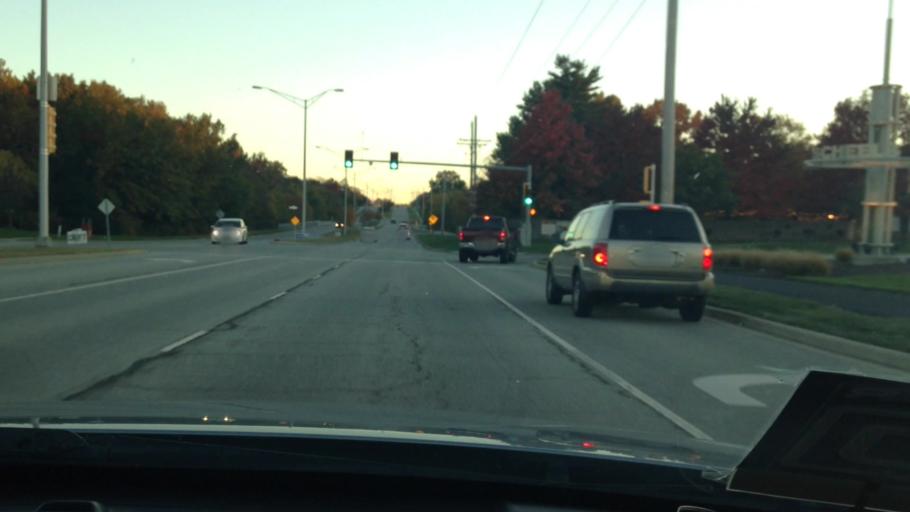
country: US
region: Kansas
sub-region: Johnson County
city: Lenexa
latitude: 38.8790
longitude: -94.7006
